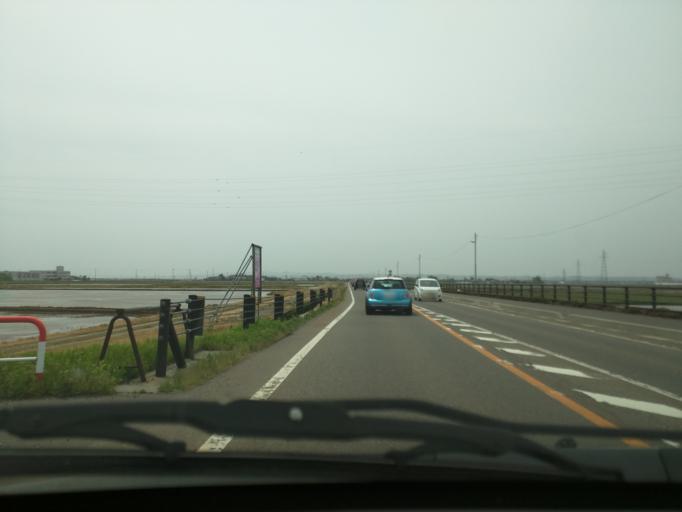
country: JP
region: Niigata
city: Mitsuke
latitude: 37.5555
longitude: 138.9273
